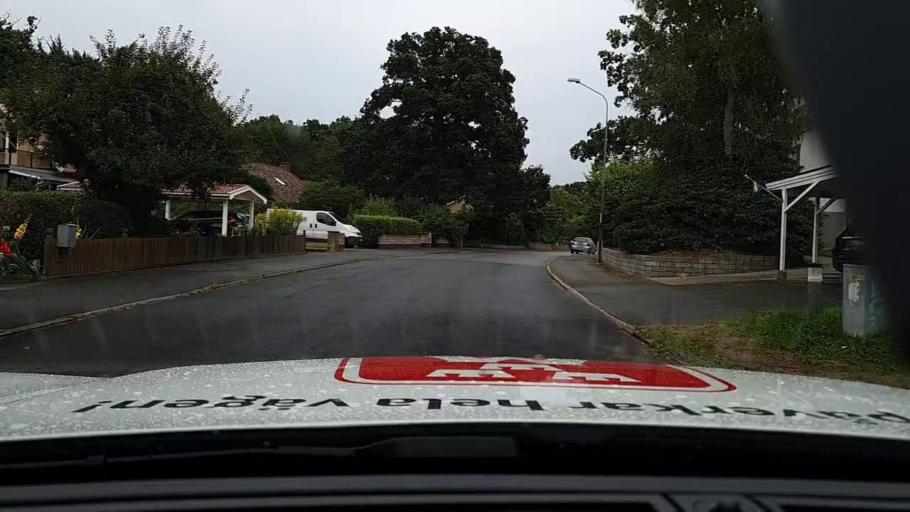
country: SE
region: Skane
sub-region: Hassleholms Kommun
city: Hassleholm
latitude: 56.1687
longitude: 13.7732
